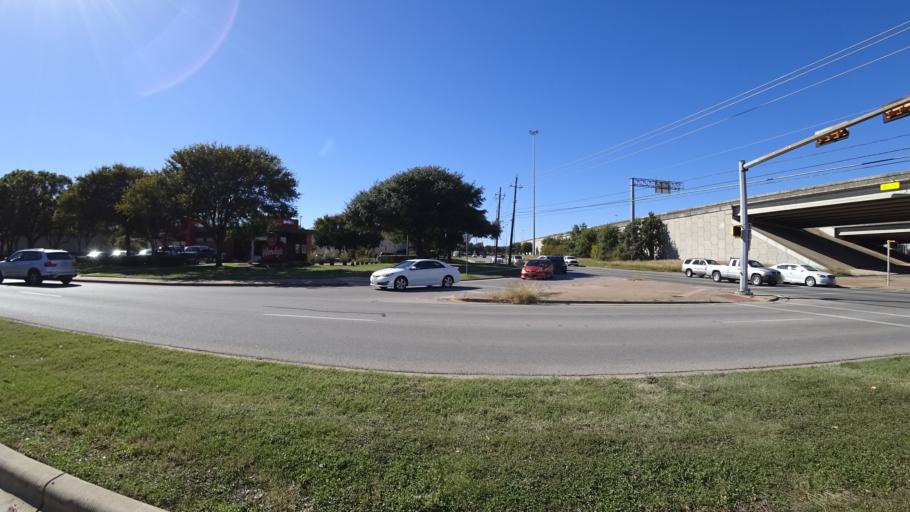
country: US
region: Texas
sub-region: Travis County
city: Rollingwood
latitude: 30.2324
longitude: -97.8185
